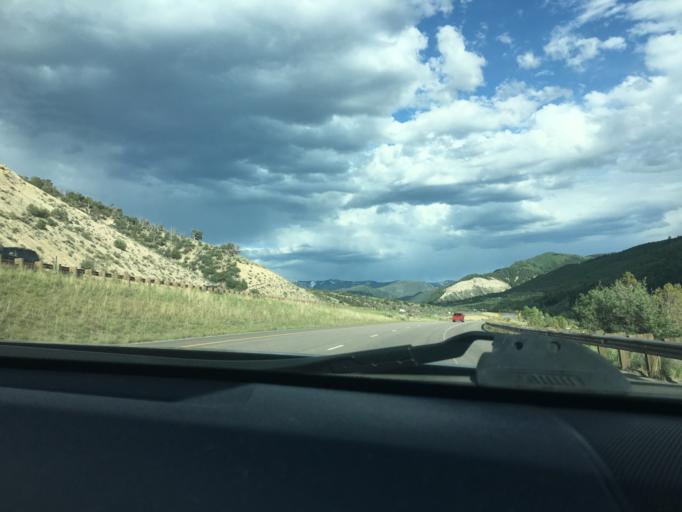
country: US
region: Colorado
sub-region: Eagle County
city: Avon
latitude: 39.6422
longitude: -106.5554
